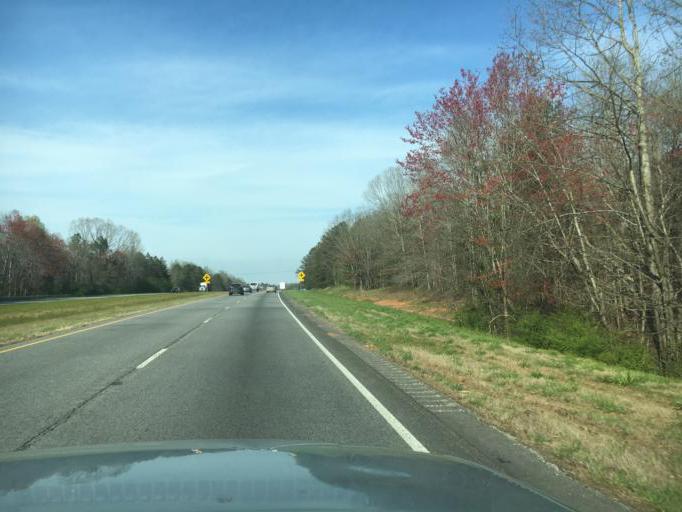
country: US
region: Georgia
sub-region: Habersham County
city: Raoul
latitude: 34.4655
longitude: -83.6019
